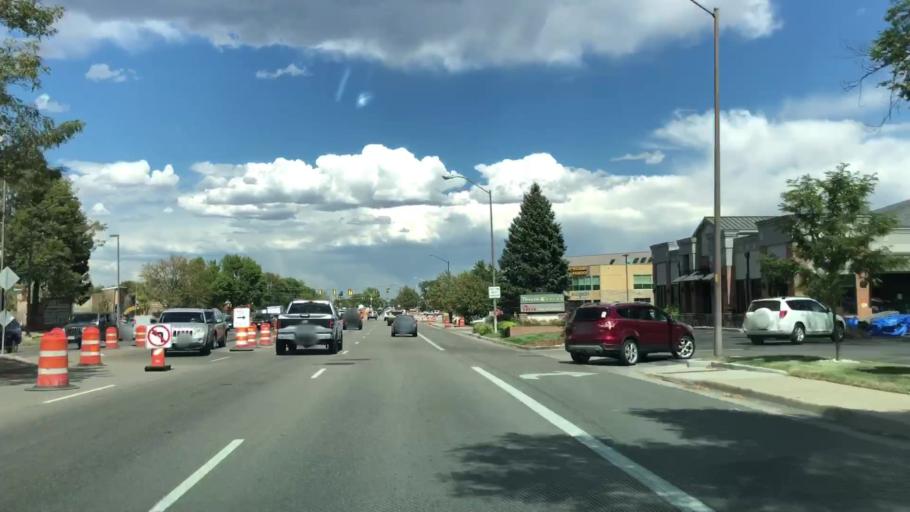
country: US
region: Colorado
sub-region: Larimer County
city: Fort Collins
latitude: 40.5361
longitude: -105.0769
